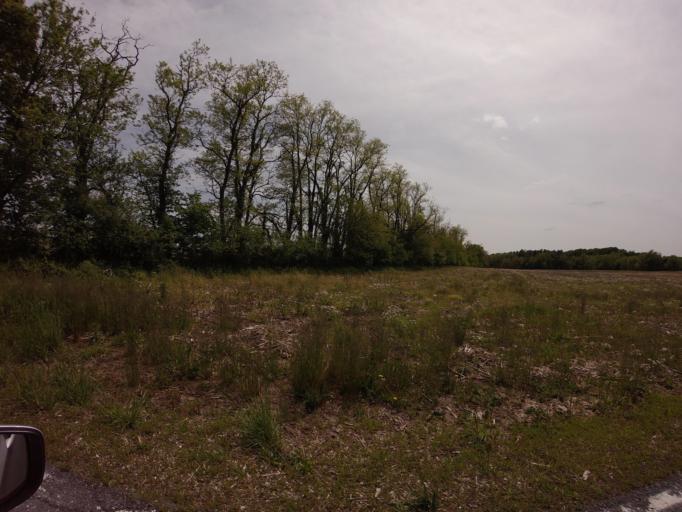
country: US
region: Maryland
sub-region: Frederick County
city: Linganore
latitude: 39.5142
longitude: -77.2209
